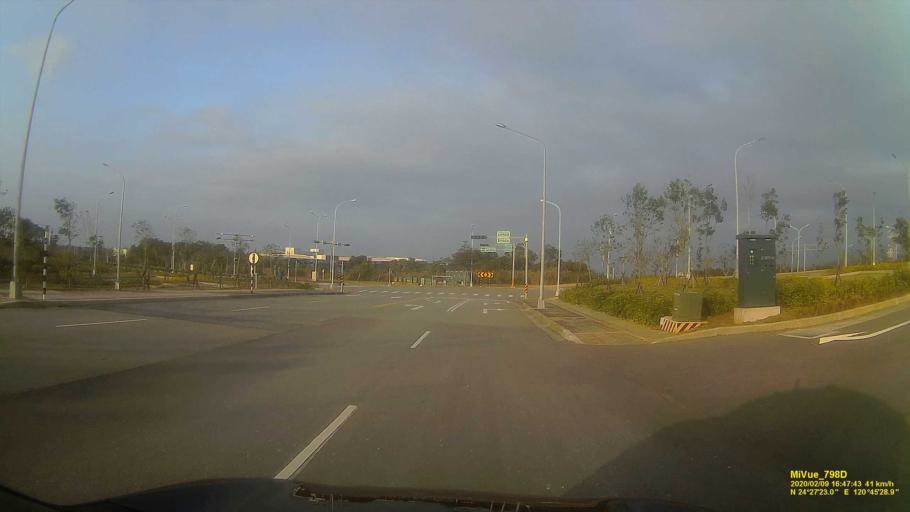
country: TW
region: Taiwan
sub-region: Miaoli
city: Miaoli
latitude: 24.4565
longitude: 120.7581
